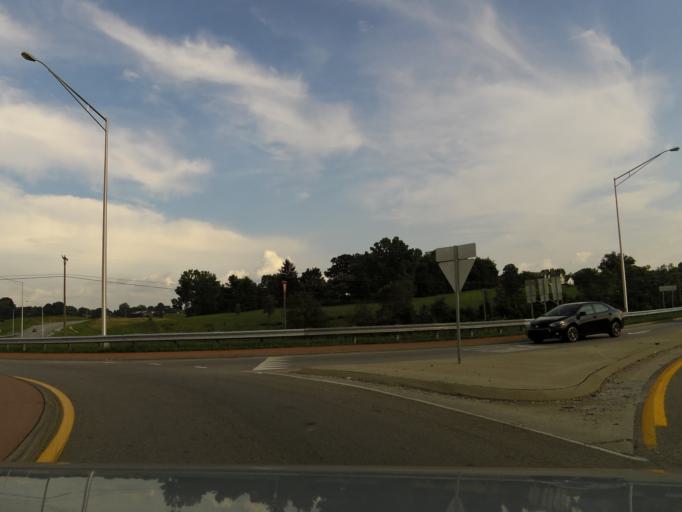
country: US
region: Kentucky
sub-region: Harrison County
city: Cynthiana
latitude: 38.3686
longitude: -84.3201
